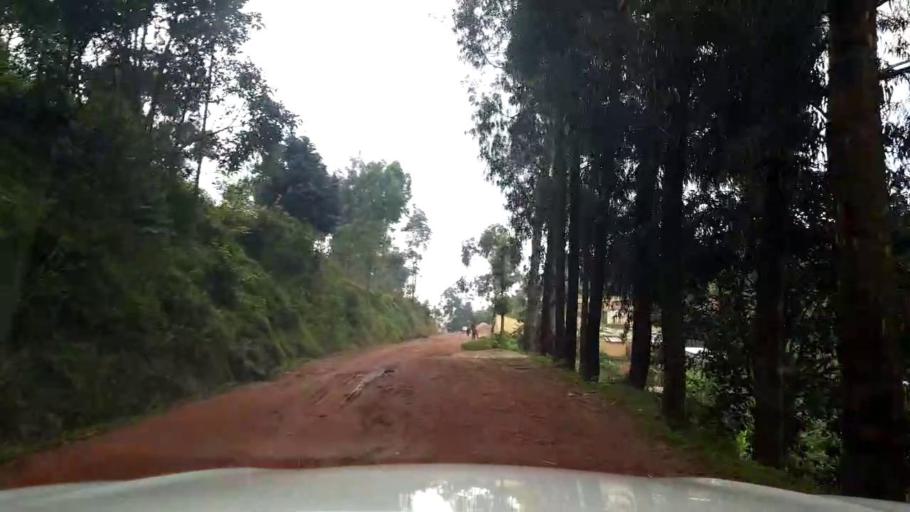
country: UG
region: Western Region
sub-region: Kisoro District
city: Kisoro
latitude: -1.4040
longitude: 29.8008
